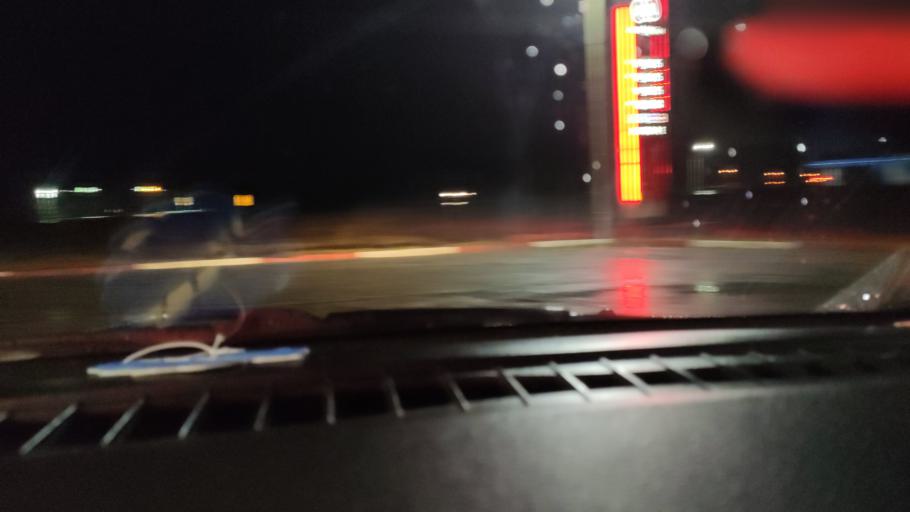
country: RU
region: Perm
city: Krasnokamsk
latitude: 58.1025
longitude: 55.7515
